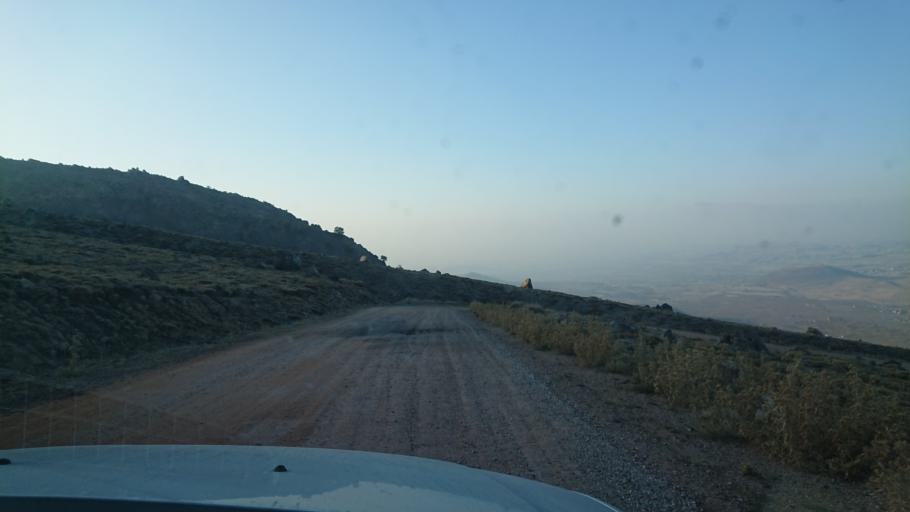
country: TR
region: Aksaray
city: Taspinar
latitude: 38.1626
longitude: 34.1770
